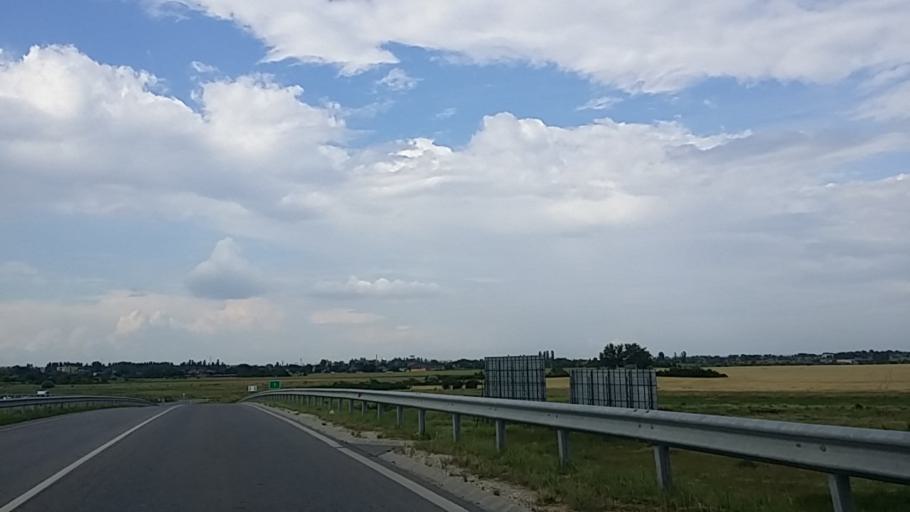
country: HU
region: Pest
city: Szigetszentmiklos
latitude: 47.3799
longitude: 19.0325
